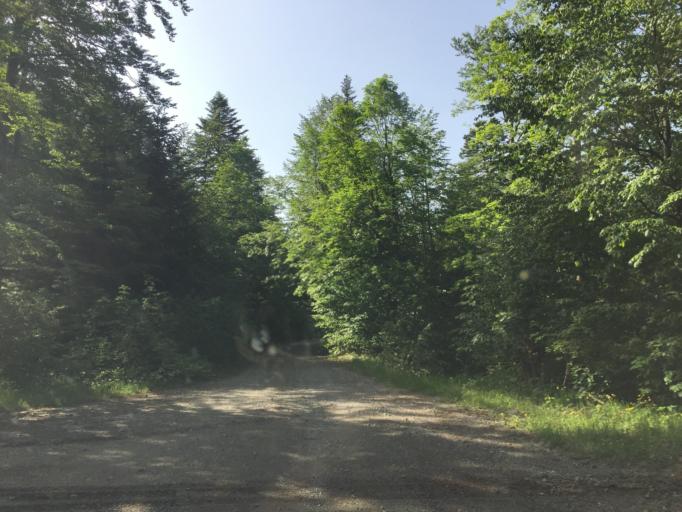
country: HR
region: Primorsko-Goranska
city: Podhum
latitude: 45.4520
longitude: 14.5530
